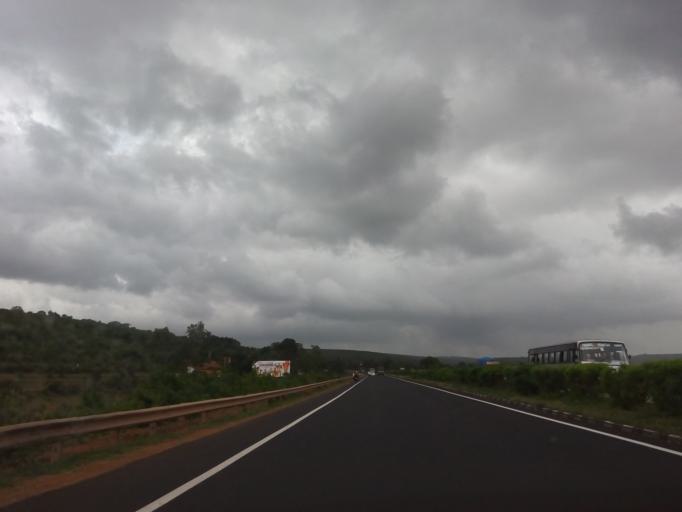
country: IN
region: Karnataka
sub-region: Belgaum
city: Hukeri
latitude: 16.0664
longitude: 74.5176
